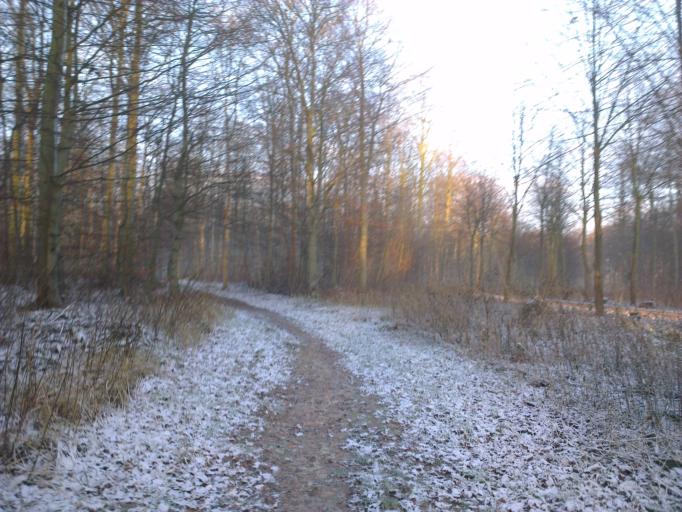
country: DK
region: Capital Region
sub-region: Frederikssund Kommune
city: Jaegerspris
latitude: 55.8641
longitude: 11.9885
